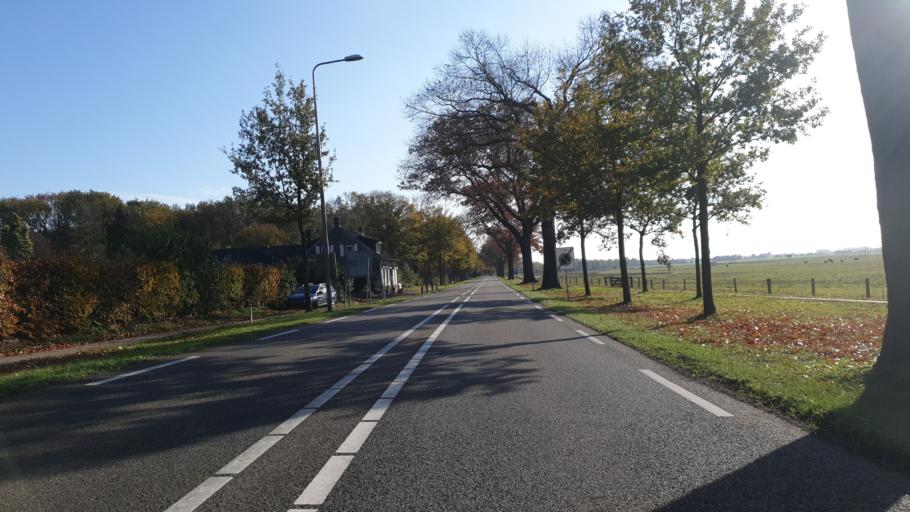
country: NL
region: Limburg
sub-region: Gemeente Venlo
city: Arcen
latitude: 51.5051
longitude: 6.1722
